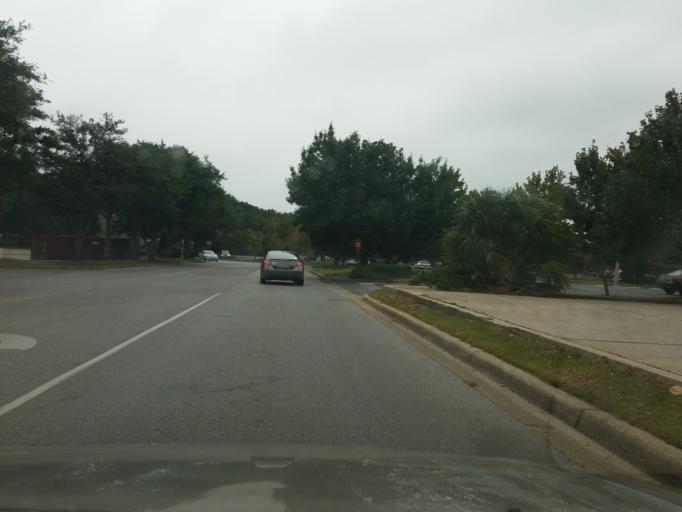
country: US
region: Florida
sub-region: Escambia County
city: Brent
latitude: 30.4726
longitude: -87.2078
